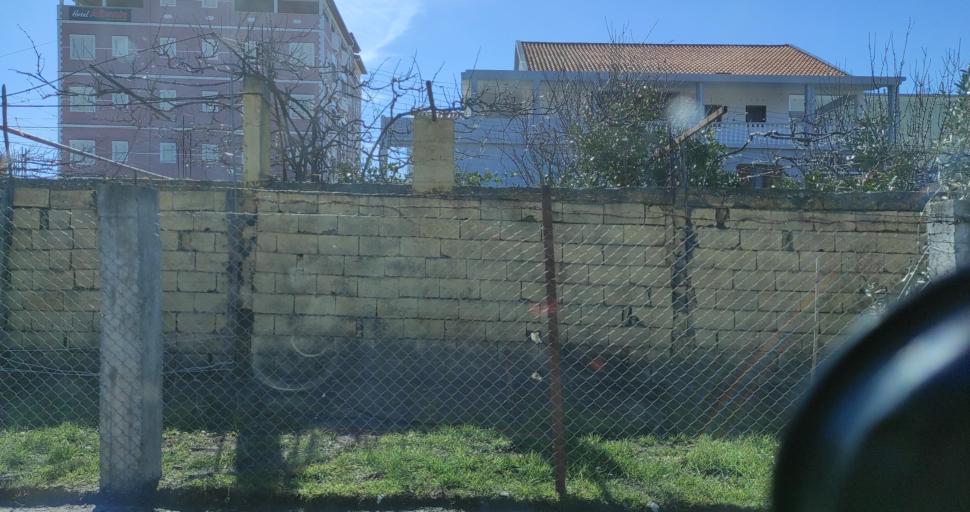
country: AL
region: Shkoder
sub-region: Rrethi i Shkodres
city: Velipoje
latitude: 41.8662
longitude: 19.4267
